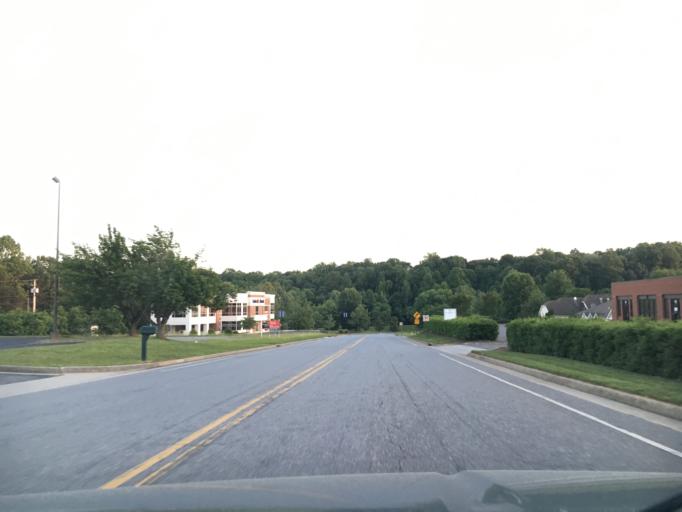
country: US
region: Virginia
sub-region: Bedford County
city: Forest
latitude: 37.3769
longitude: -79.2453
